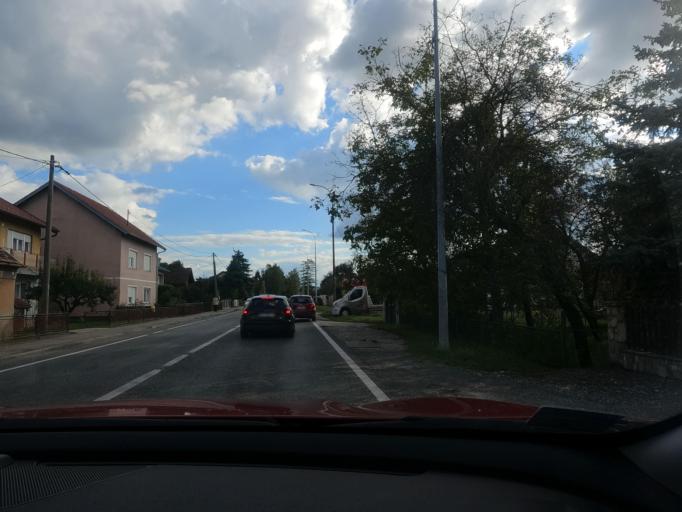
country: HR
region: Sisacko-Moslavacka
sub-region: Grad Sisak
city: Sisak
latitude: 45.4518
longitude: 16.3704
